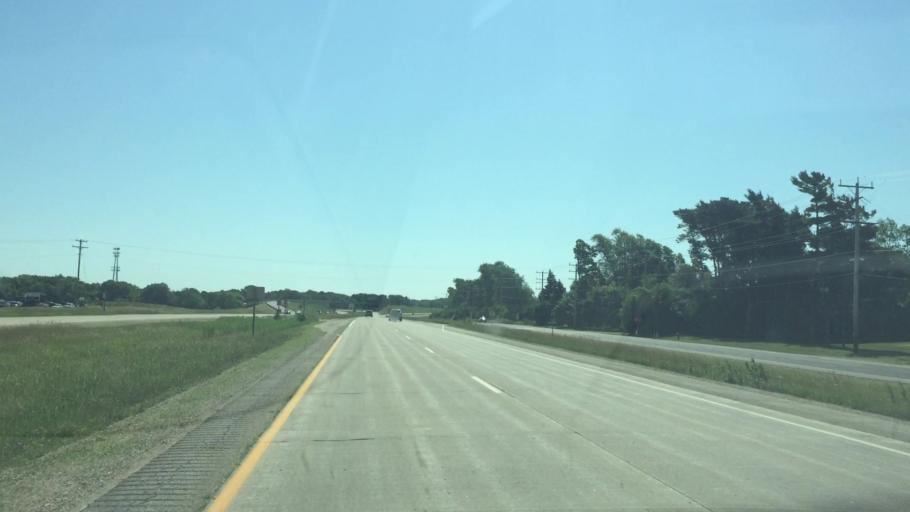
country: US
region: Wisconsin
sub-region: Outagamie County
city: Kimberly
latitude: 44.2075
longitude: -88.3450
